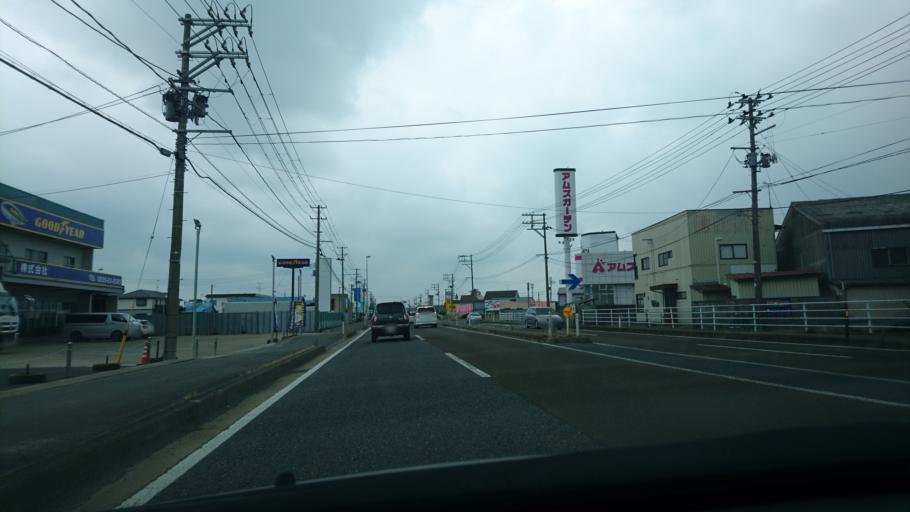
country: JP
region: Miyagi
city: Furukawa
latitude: 38.5885
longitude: 140.9409
